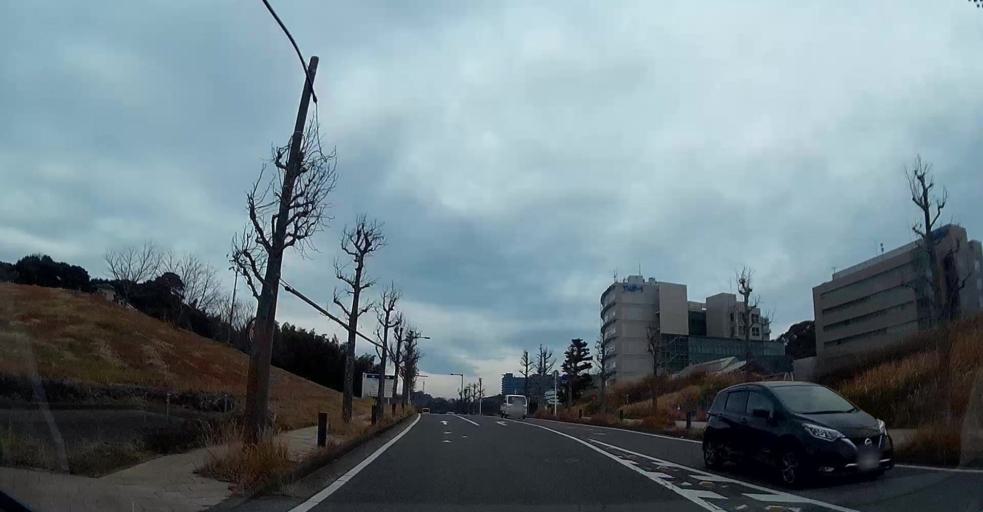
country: JP
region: Kanagawa
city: Yokosuka
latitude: 35.2228
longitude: 139.6756
